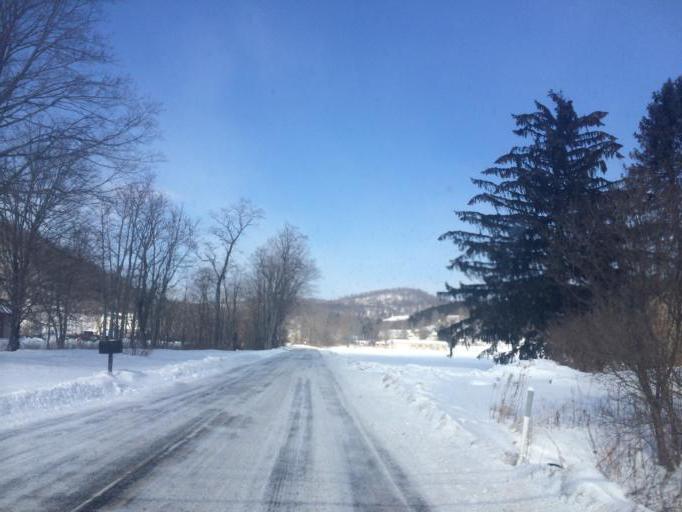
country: US
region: Pennsylvania
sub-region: Centre County
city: Stormstown
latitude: 40.8396
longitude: -77.9961
